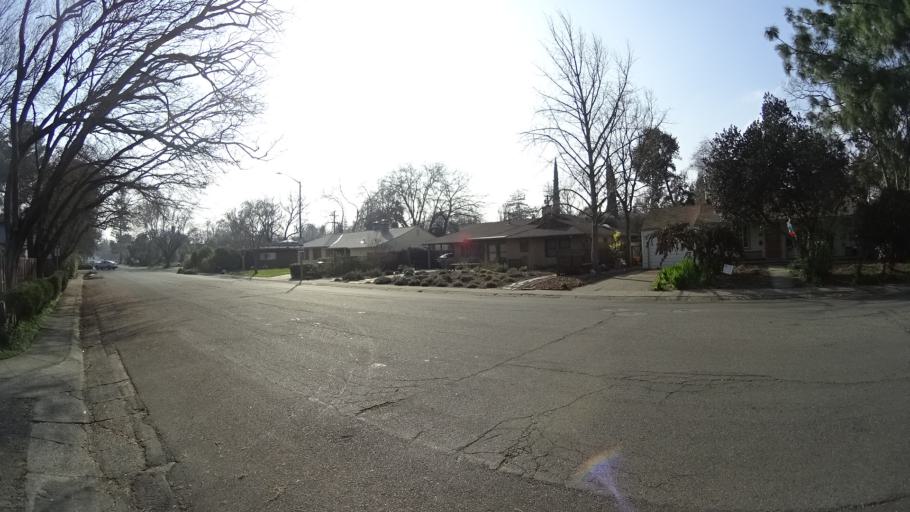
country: US
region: California
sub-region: Yolo County
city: Davis
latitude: 38.5500
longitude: -121.7477
